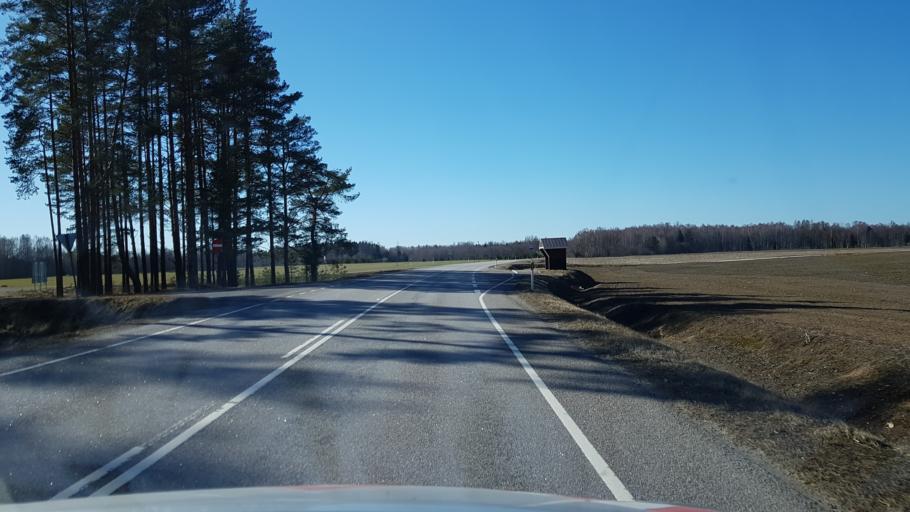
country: EE
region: Laeaene-Virumaa
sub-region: Viru-Nigula vald
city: Kunda
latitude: 59.3607
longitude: 26.6263
